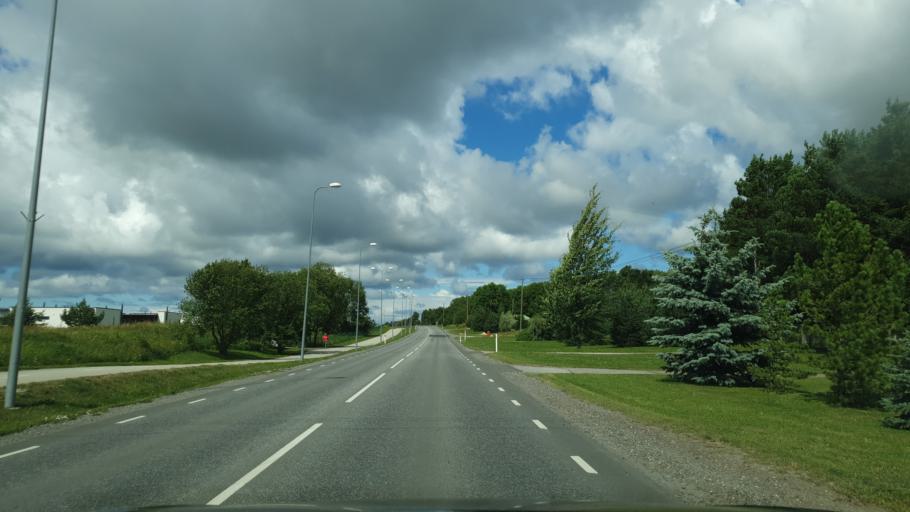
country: EE
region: Harju
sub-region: Viimsi vald
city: Viimsi
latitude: 59.4974
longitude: 24.8731
